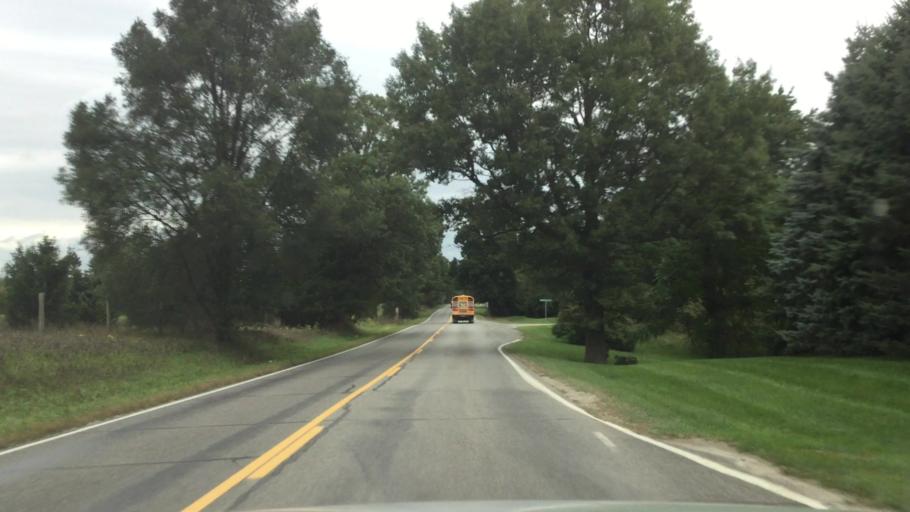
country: US
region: Michigan
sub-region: Livingston County
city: Brighton
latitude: 42.4837
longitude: -83.7675
